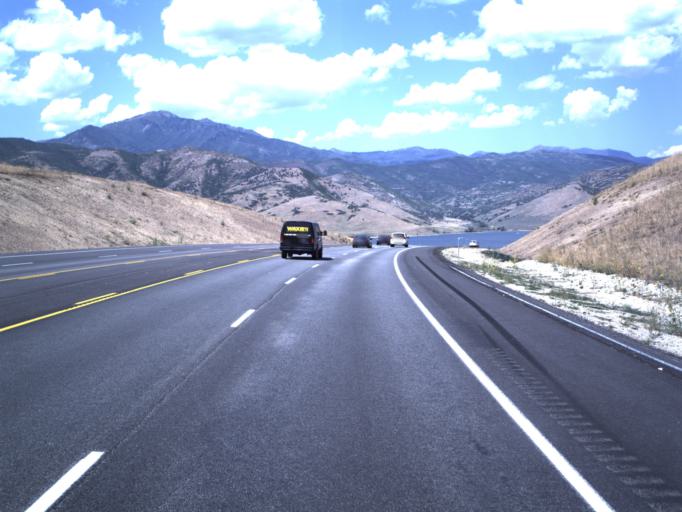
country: US
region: Utah
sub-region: Wasatch County
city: Midway
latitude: 40.4180
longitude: -111.4882
